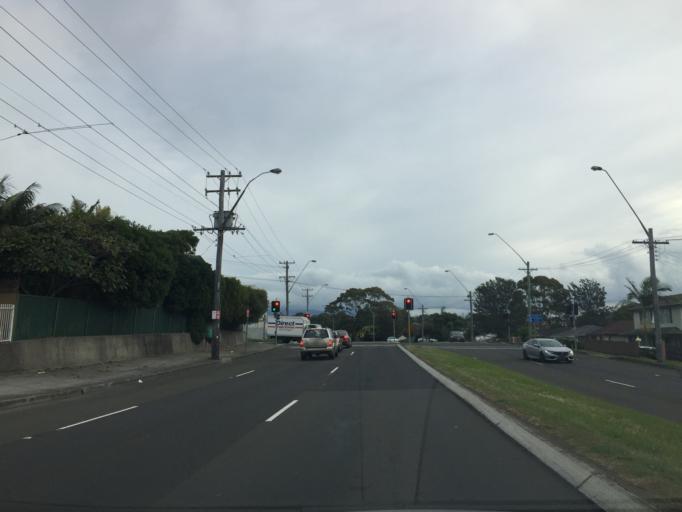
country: AU
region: New South Wales
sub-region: Shellharbour
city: Barrack Heights
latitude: -34.5560
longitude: 150.8480
